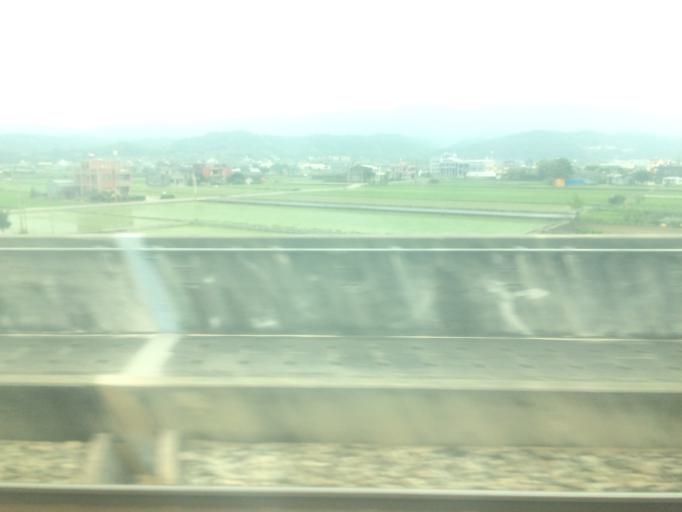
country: TW
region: Taiwan
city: Fengyuan
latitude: 24.3980
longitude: 120.6885
